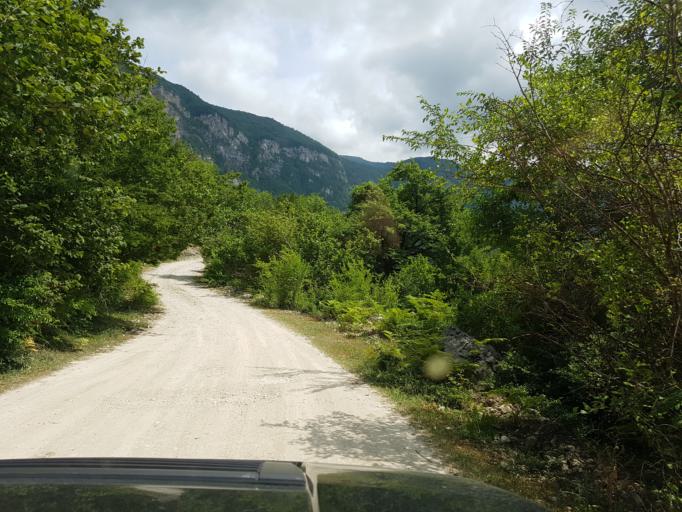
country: GE
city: Tqibuli
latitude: 42.5202
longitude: 42.8010
